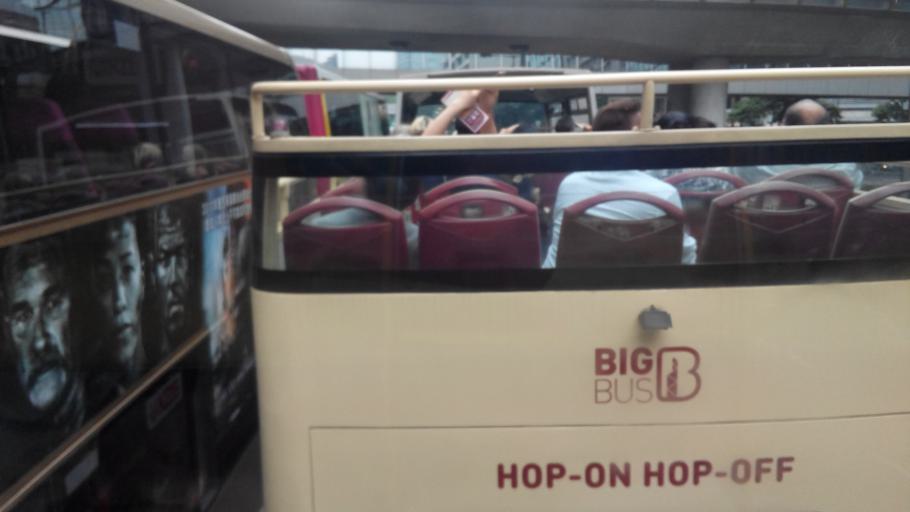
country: HK
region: Central and Western
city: Central
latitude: 22.2803
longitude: 114.1569
